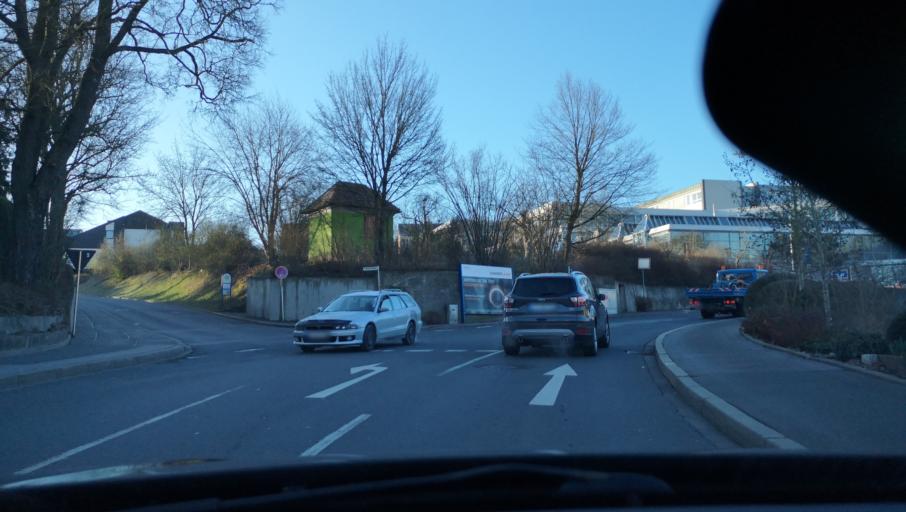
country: DE
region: Bavaria
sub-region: Upper Franconia
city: Lichtenfels
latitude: 50.1465
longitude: 11.0669
